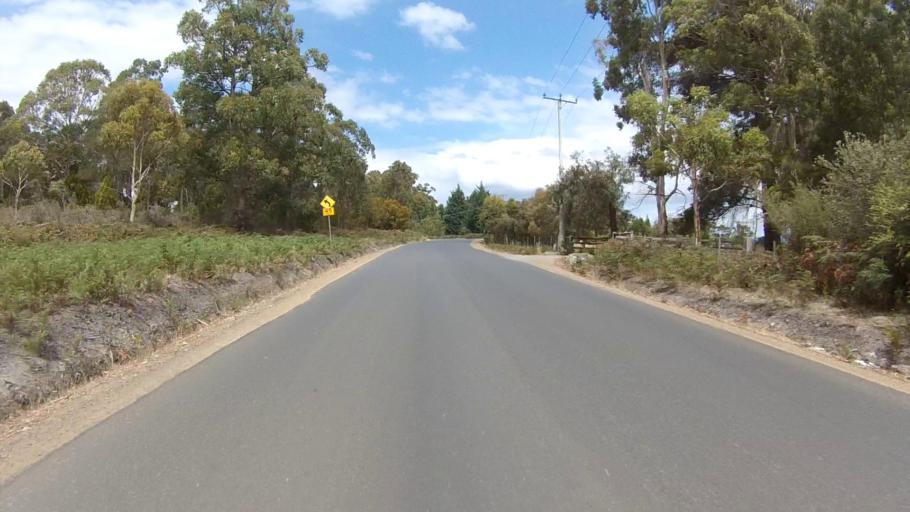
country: AU
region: Tasmania
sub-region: Kingborough
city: Blackmans Bay
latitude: -43.0113
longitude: 147.2883
